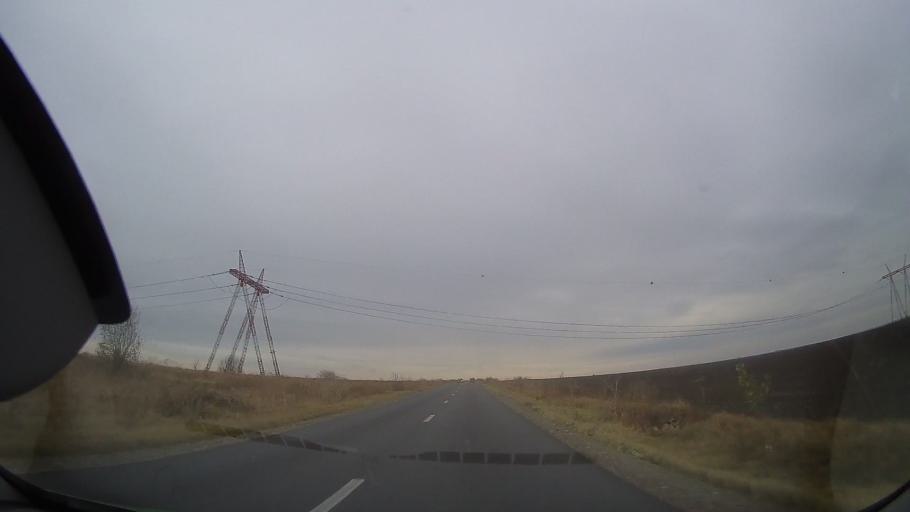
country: RO
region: Ialomita
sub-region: Oras Amara
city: Amara
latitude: 44.6396
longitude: 27.3007
